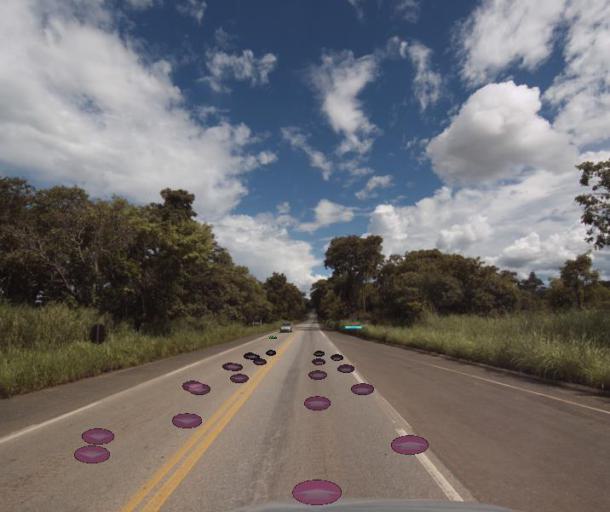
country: BR
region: Goias
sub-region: Porangatu
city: Porangatu
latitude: -13.8679
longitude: -49.0519
